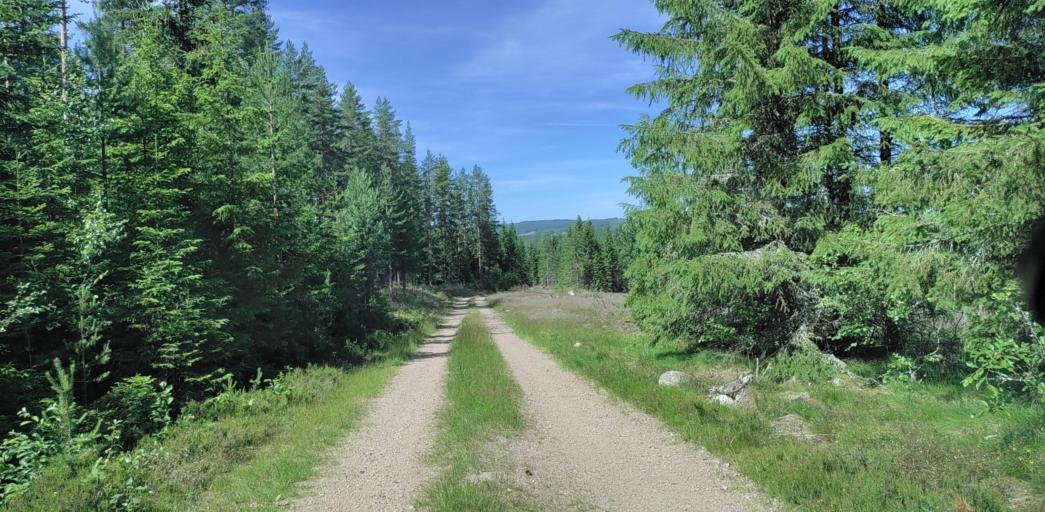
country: SE
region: Vaermland
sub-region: Hagfors Kommun
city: Ekshaerad
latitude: 60.0941
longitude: 13.3741
